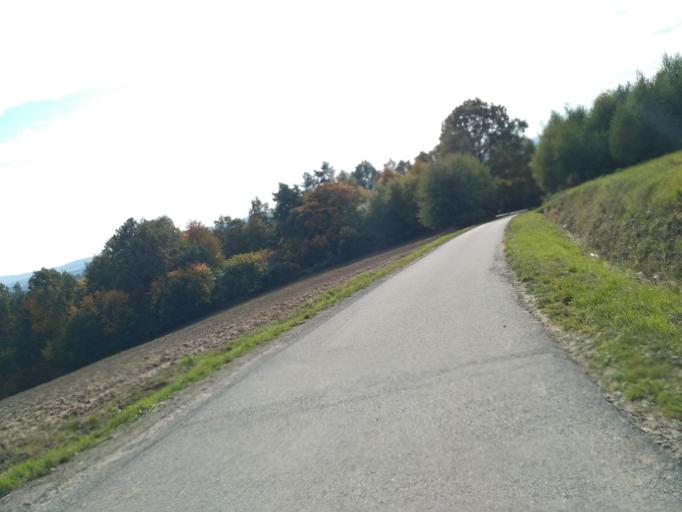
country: PL
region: Subcarpathian Voivodeship
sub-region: Powiat debicki
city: Slotowa
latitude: 49.9313
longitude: 21.2752
